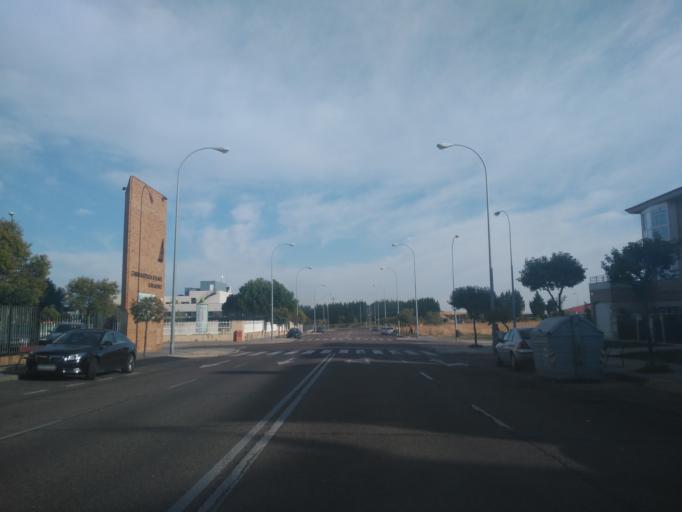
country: ES
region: Castille and Leon
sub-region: Provincia de Salamanca
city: Salamanca
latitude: 40.9828
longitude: -5.6663
